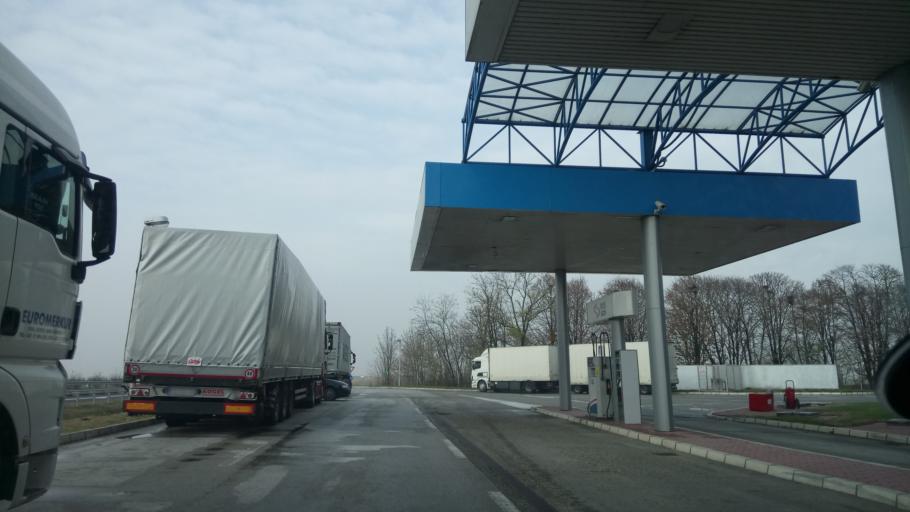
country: RS
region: Autonomna Pokrajina Vojvodina
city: Nova Pazova
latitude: 44.9713
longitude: 20.2332
